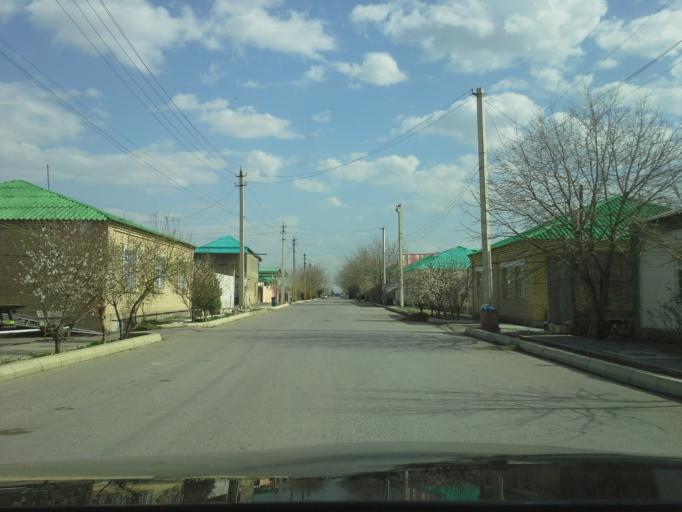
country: TM
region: Ahal
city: Abadan
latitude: 37.9885
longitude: 58.2790
